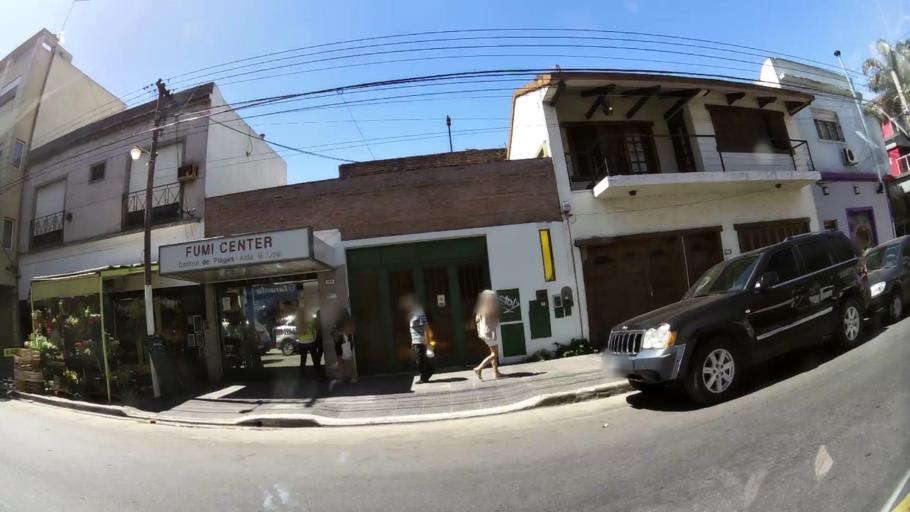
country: AR
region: Buenos Aires
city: Caseros
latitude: -34.5983
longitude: -58.5434
